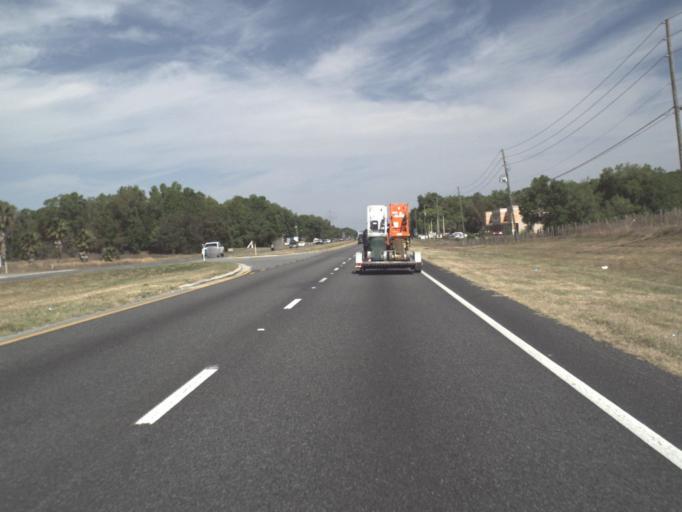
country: US
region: Florida
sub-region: Marion County
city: Belleview
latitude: 29.0204
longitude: -82.0153
